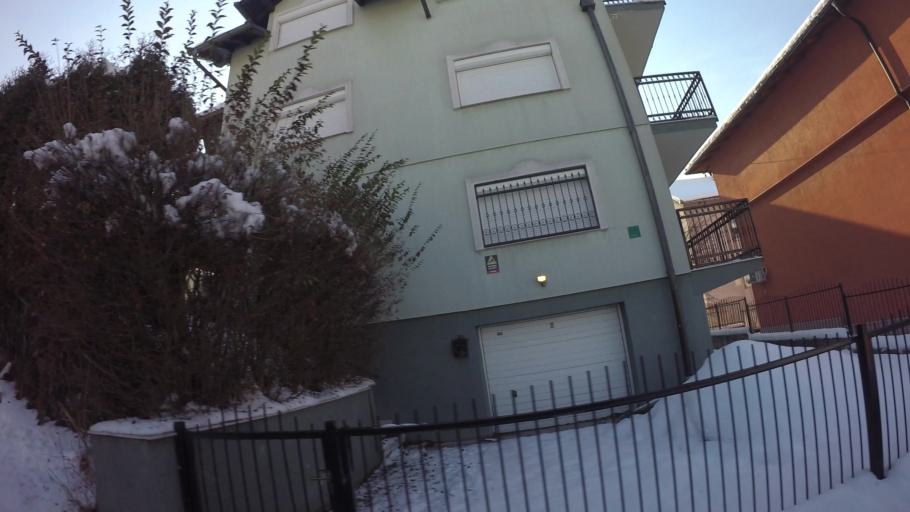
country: BA
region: Federation of Bosnia and Herzegovina
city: Kobilja Glava
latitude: 43.8485
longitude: 18.4047
